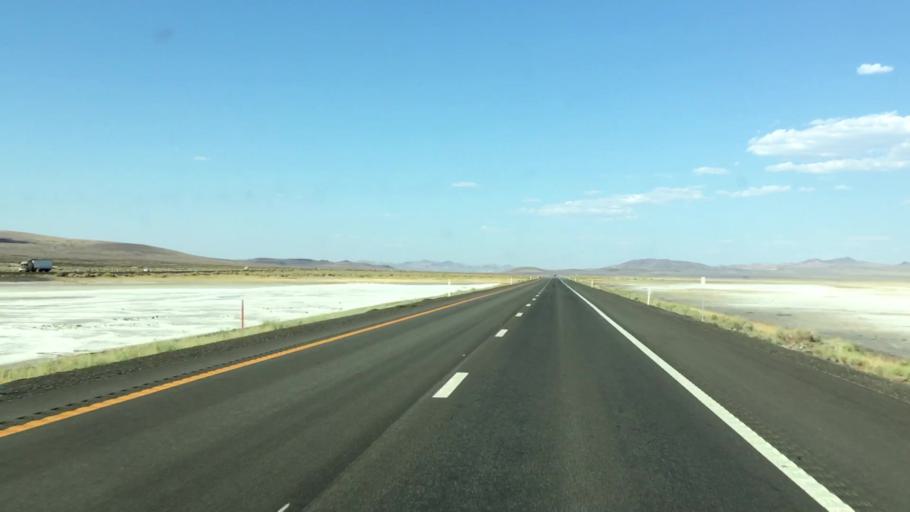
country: US
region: Nevada
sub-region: Lyon County
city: Fernley
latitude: 39.7057
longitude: -119.0946
